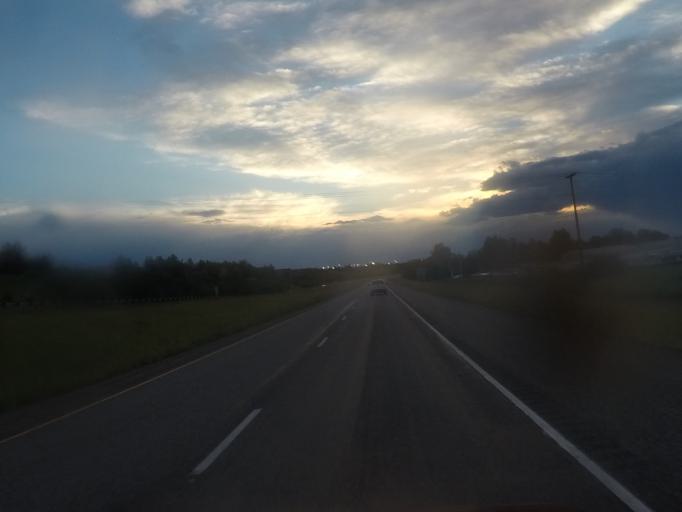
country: US
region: Montana
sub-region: Gallatin County
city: Bozeman
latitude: 45.6712
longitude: -110.9999
